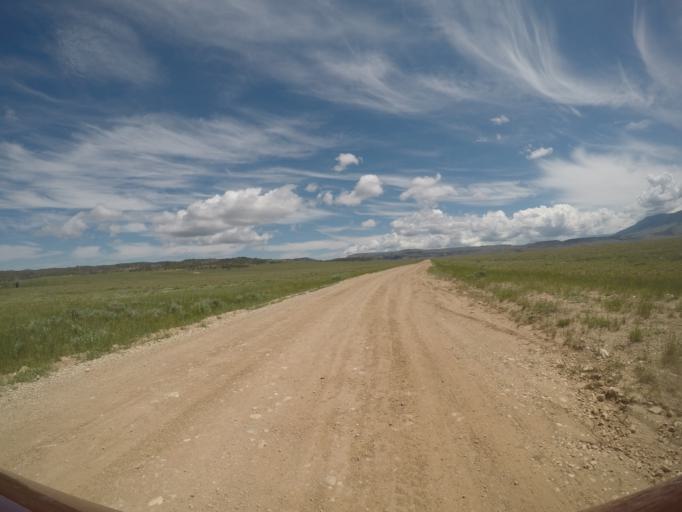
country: US
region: Montana
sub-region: Yellowstone County
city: Laurel
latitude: 45.2320
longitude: -108.6993
